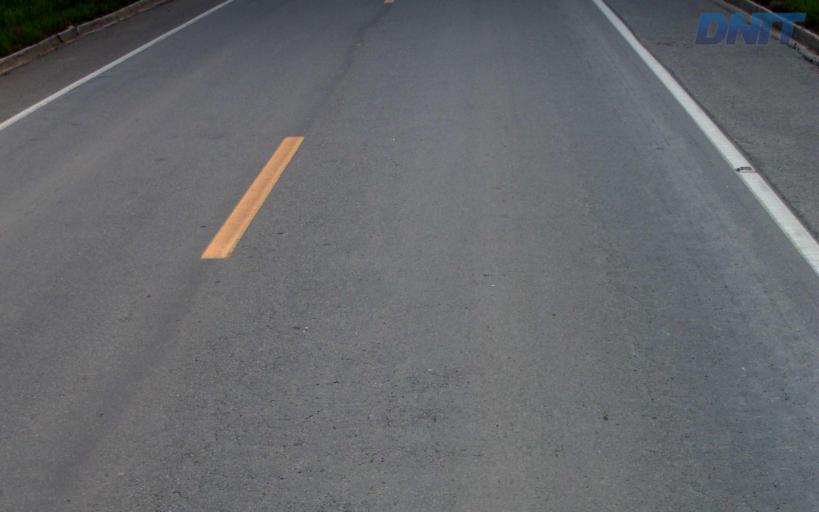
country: BR
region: Minas Gerais
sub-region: Governador Valadares
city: Governador Valadares
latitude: -18.9823
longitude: -42.1044
